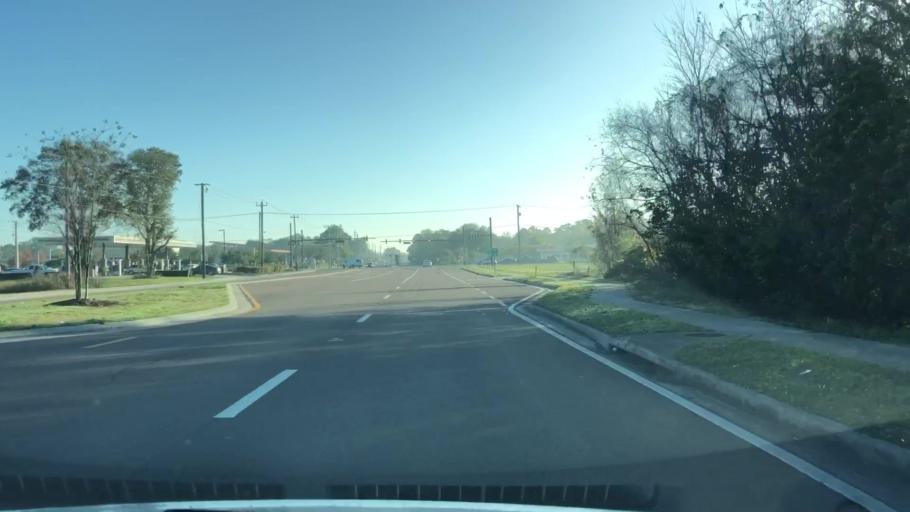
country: US
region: Florida
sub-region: Seminole County
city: Sanford
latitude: 28.7864
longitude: -81.2995
